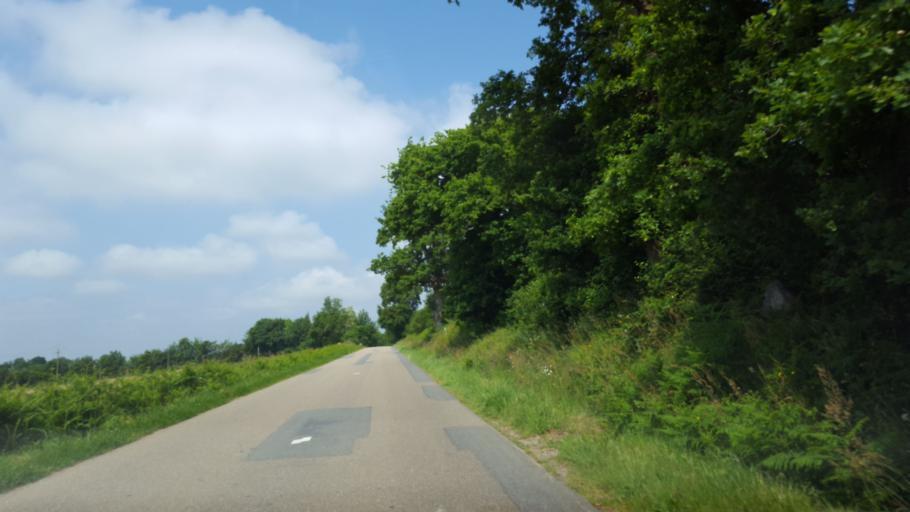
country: FR
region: Brittany
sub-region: Departement d'Ille-et-Vilaine
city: Guignen
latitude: 47.9277
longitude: -1.8983
